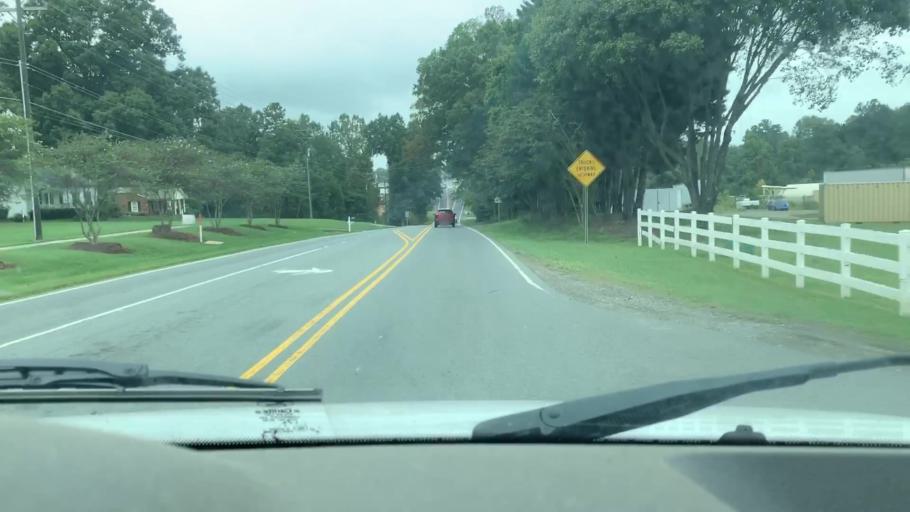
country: US
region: North Carolina
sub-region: Mecklenburg County
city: Huntersville
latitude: 35.4347
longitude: -80.8438
